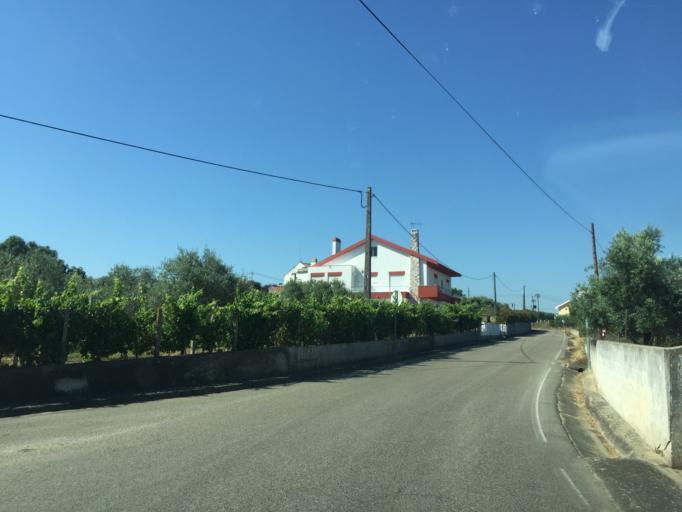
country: PT
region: Santarem
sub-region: Tomar
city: Tomar
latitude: 39.5771
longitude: -8.3242
